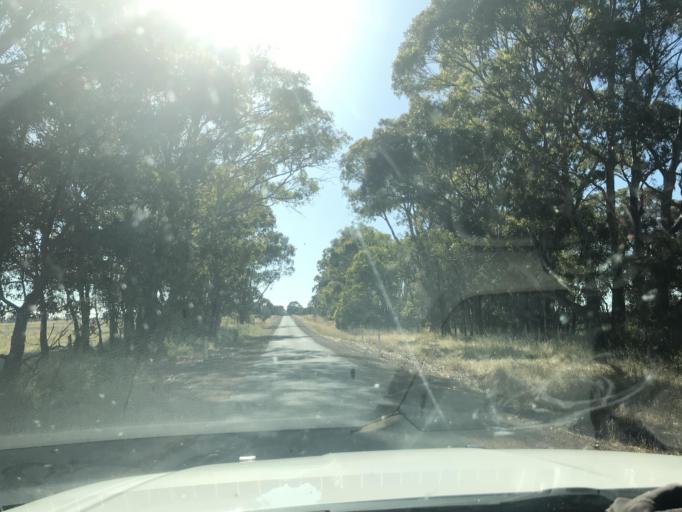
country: AU
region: Victoria
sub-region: Horsham
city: Horsham
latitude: -37.0062
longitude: 141.6323
